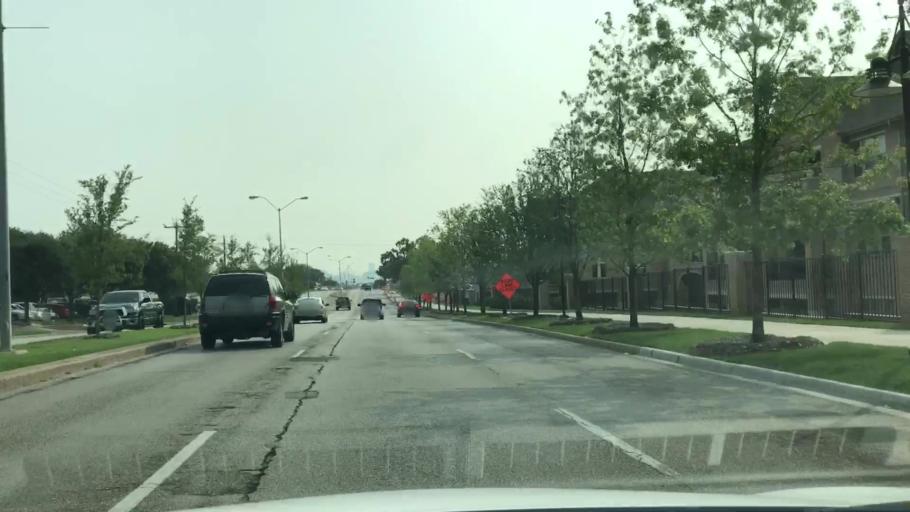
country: US
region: Texas
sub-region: Dallas County
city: Cockrell Hill
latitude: 32.7592
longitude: -96.8625
